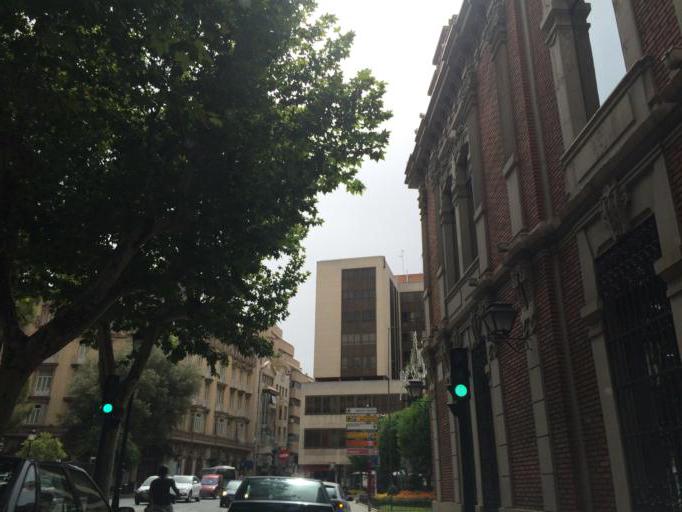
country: ES
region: Castille-La Mancha
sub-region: Provincia de Albacete
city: Albacete
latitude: 38.9953
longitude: -1.8535
